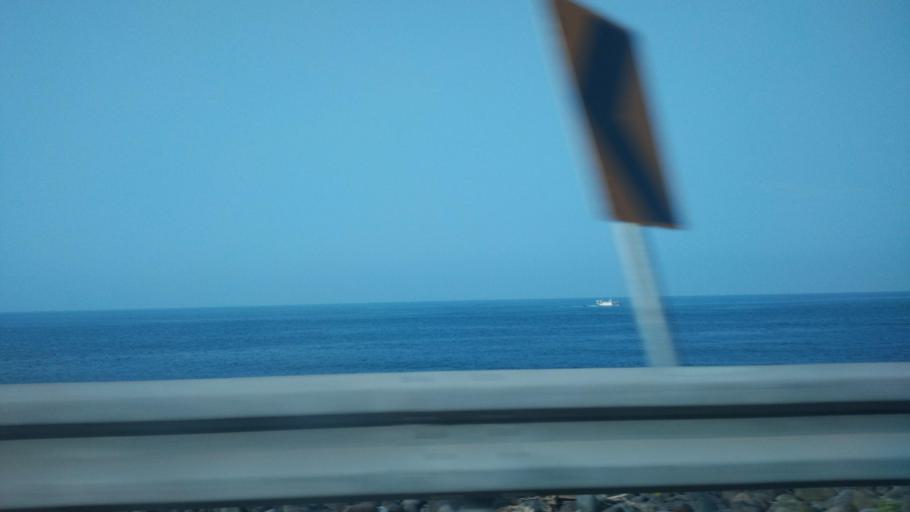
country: TW
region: Taiwan
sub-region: Keelung
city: Keelung
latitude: 25.2775
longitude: 121.6174
